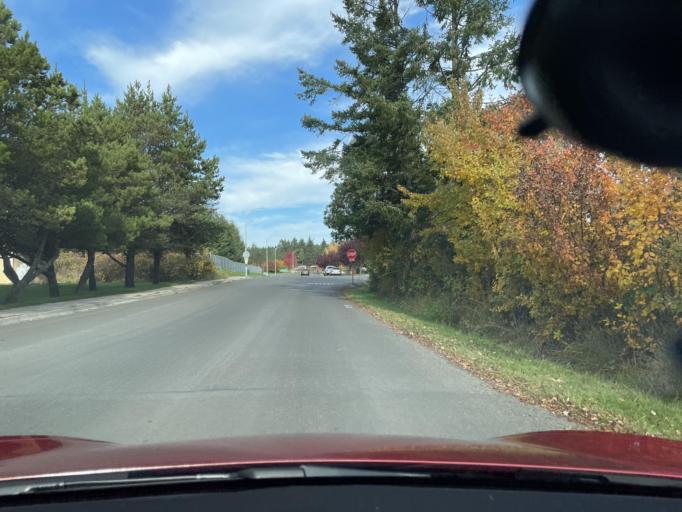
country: US
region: Washington
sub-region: San Juan County
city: Friday Harbor
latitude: 48.5394
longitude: -123.0286
